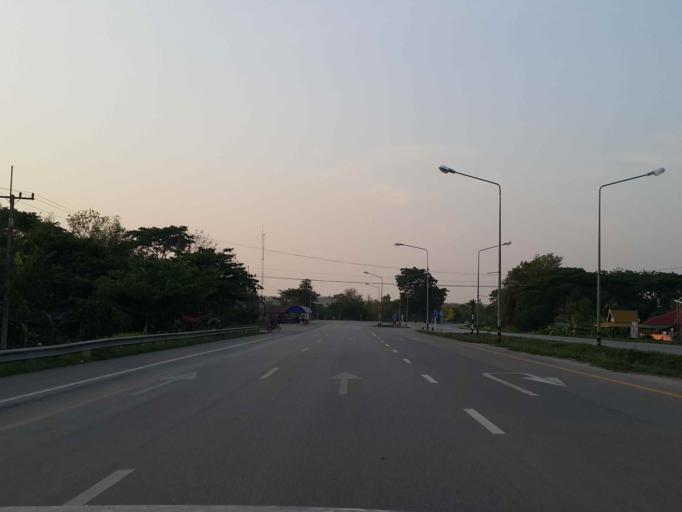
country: TH
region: Lampang
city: Sop Prap
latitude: 17.9499
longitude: 99.3510
